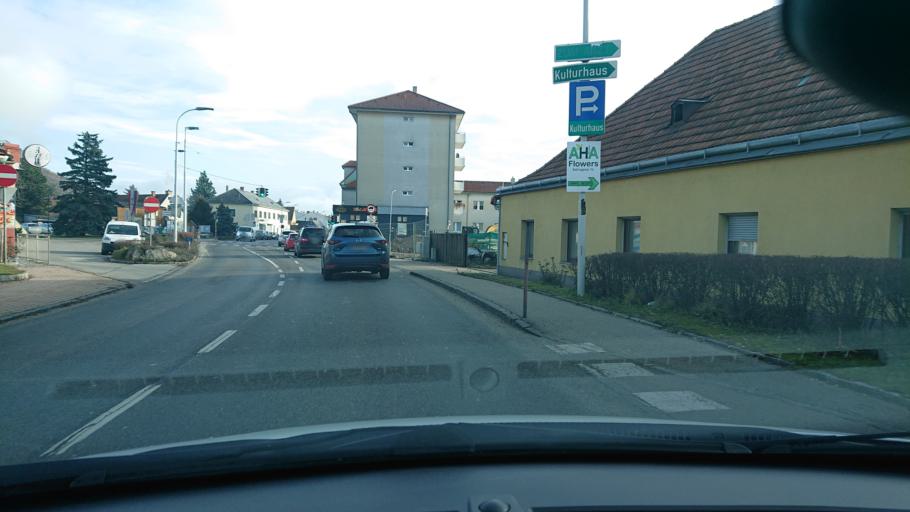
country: AT
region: Lower Austria
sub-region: Politischer Bezirk Baden
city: Hirtenberg
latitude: 47.9308
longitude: 16.1751
